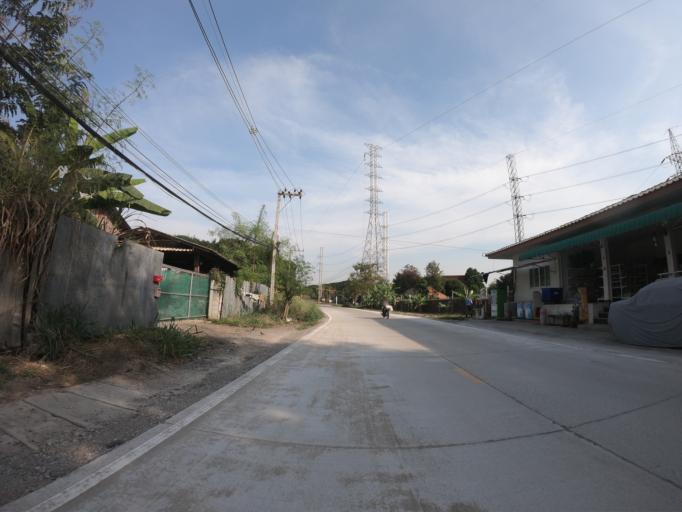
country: TH
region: Chiang Mai
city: Chiang Mai
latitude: 18.8191
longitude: 99.0138
